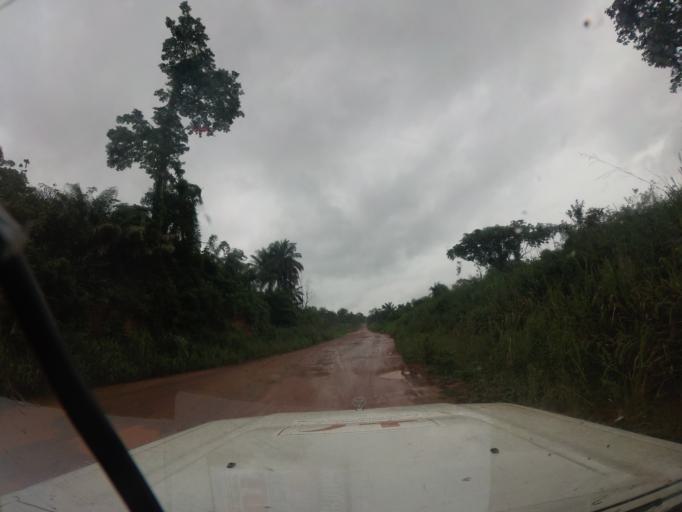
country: SL
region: Eastern Province
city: Tefeya
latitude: 8.5701
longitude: -11.2885
